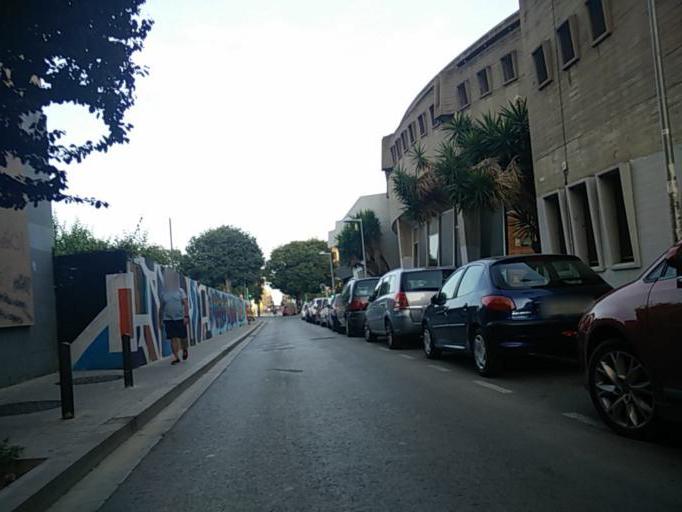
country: ES
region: Catalonia
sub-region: Provincia de Barcelona
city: Badalona
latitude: 41.4449
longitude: 2.2372
